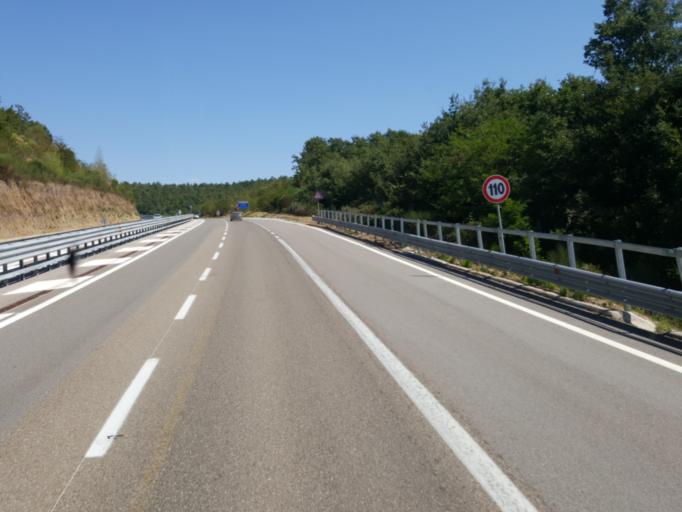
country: IT
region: Tuscany
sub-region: Provincia di Grosseto
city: Civitella Marittima
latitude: 42.9463
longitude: 11.2783
